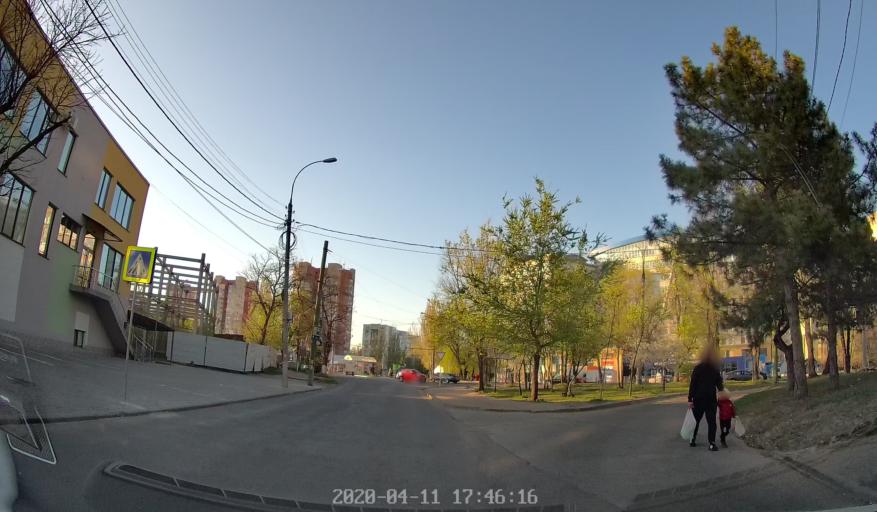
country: MD
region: Chisinau
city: Chisinau
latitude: 46.9907
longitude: 28.8207
